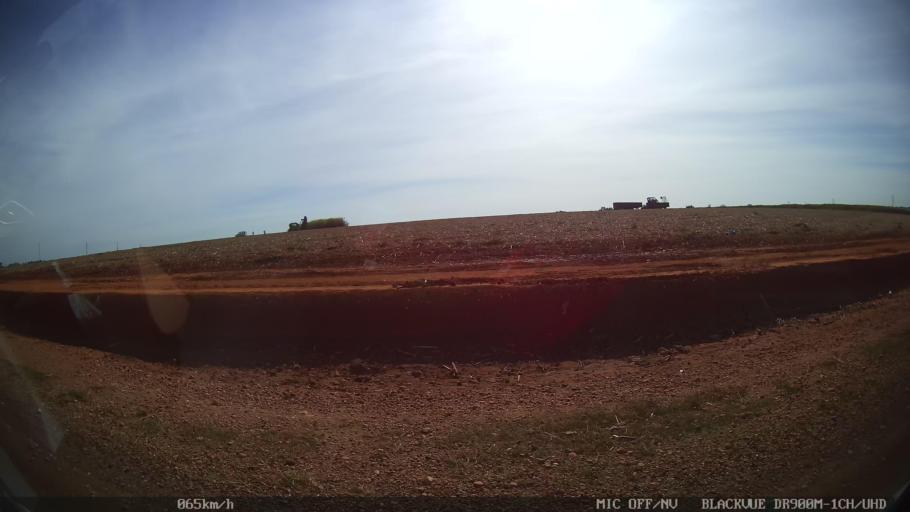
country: BR
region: Sao Paulo
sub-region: Piracicaba
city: Piracicaba
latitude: -22.7896
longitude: -47.6445
